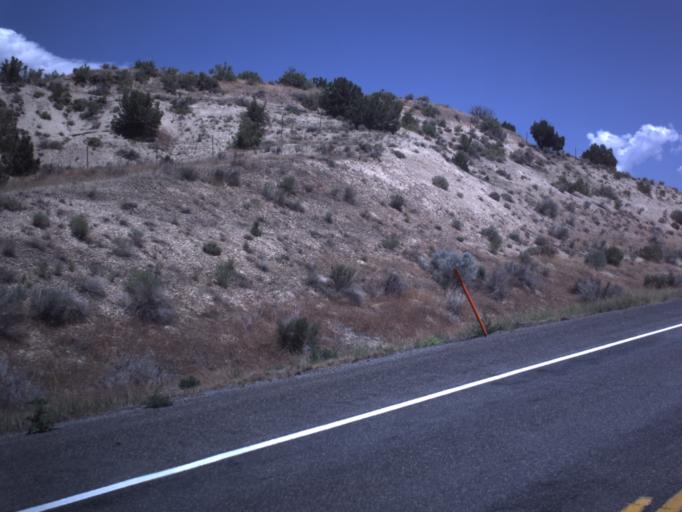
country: US
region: Utah
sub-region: Juab County
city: Nephi
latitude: 39.5701
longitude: -112.1902
